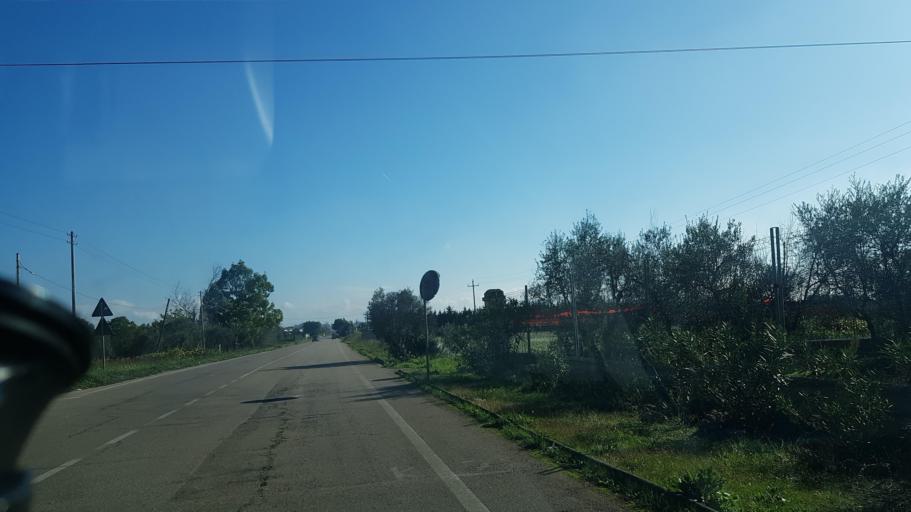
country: IT
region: Apulia
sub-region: Provincia di Lecce
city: Novoli
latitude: 40.3800
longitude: 18.0352
